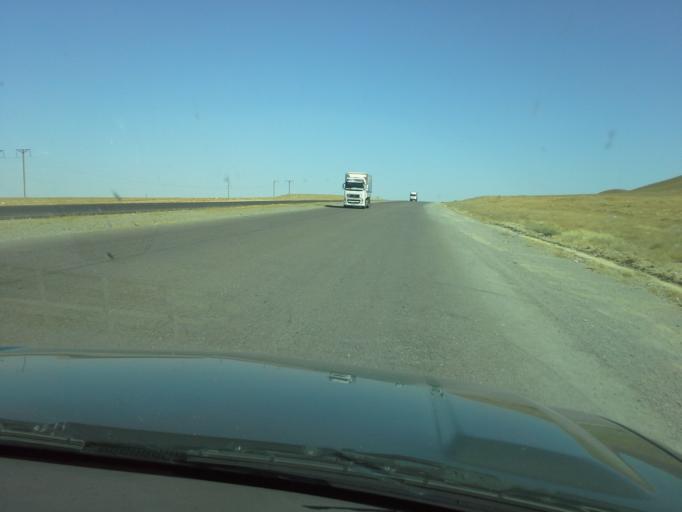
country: TM
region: Ahal
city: Baharly
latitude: 38.5929
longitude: 57.0957
